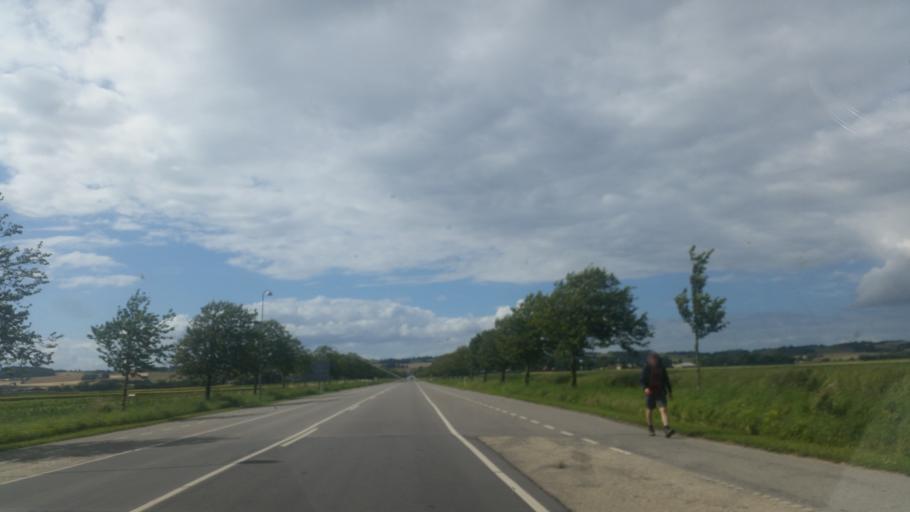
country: DK
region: Zealand
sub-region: Odsherred Kommune
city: Horve
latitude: 55.7926
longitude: 11.4572
